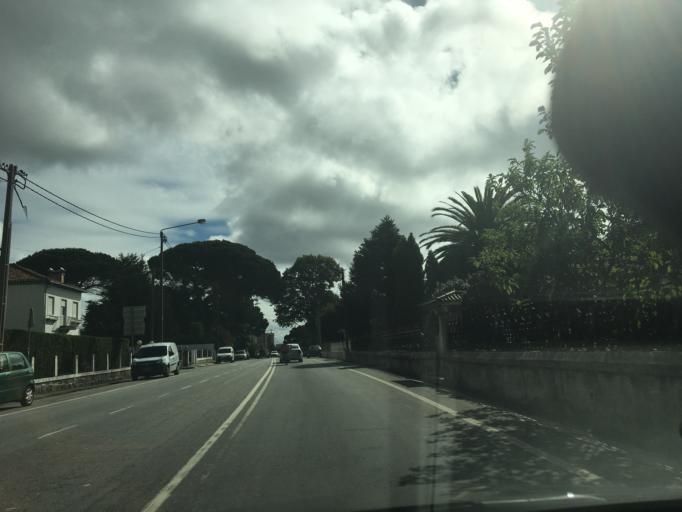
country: PT
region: Porto
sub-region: Maia
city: Gemunde
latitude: 41.2541
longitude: -8.6537
